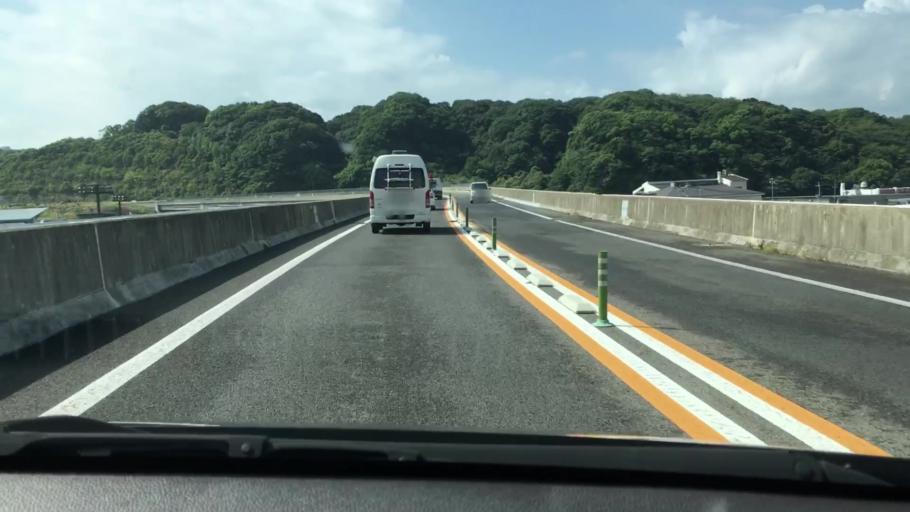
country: JP
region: Nagasaki
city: Sasebo
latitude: 33.1571
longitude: 129.7295
